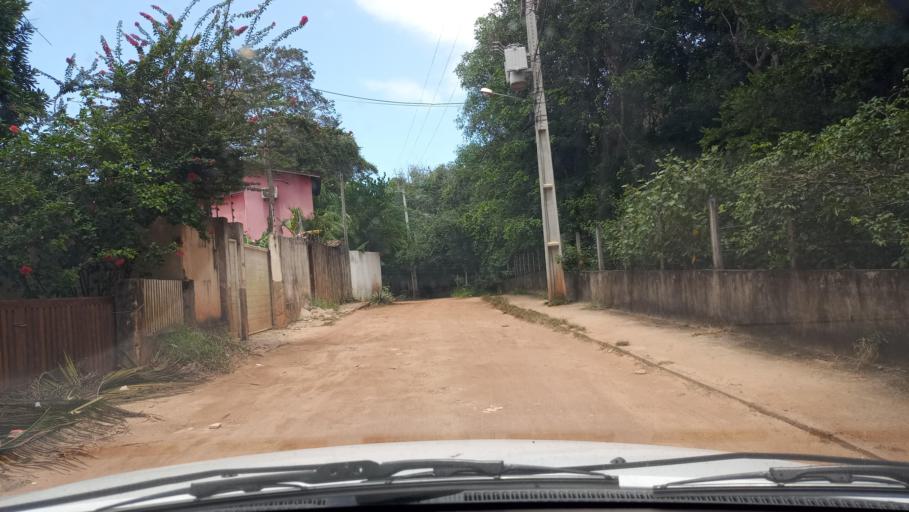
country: BR
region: Rio Grande do Norte
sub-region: Ares
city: Ares
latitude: -6.2367
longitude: -35.0462
